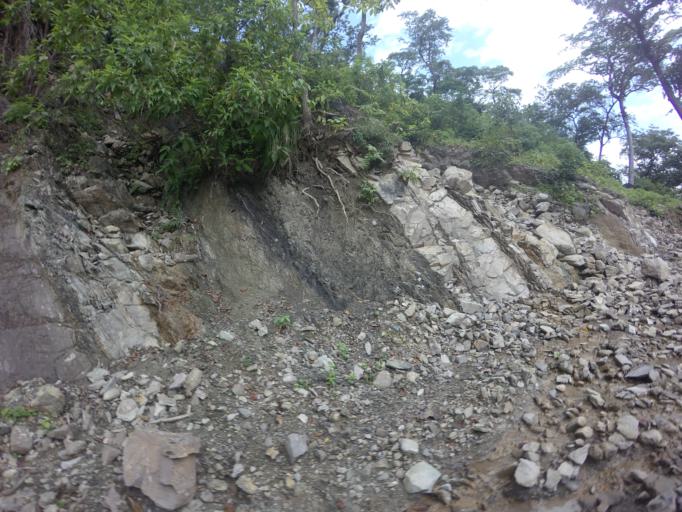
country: NP
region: Far Western
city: Tikapur
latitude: 28.6516
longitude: 81.2868
